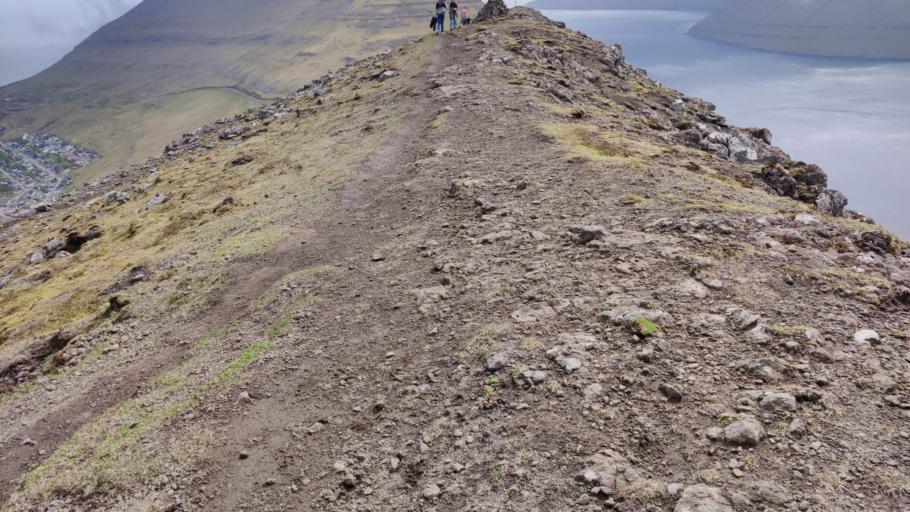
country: FO
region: Nordoyar
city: Klaksvik
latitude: 62.2368
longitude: -6.6172
